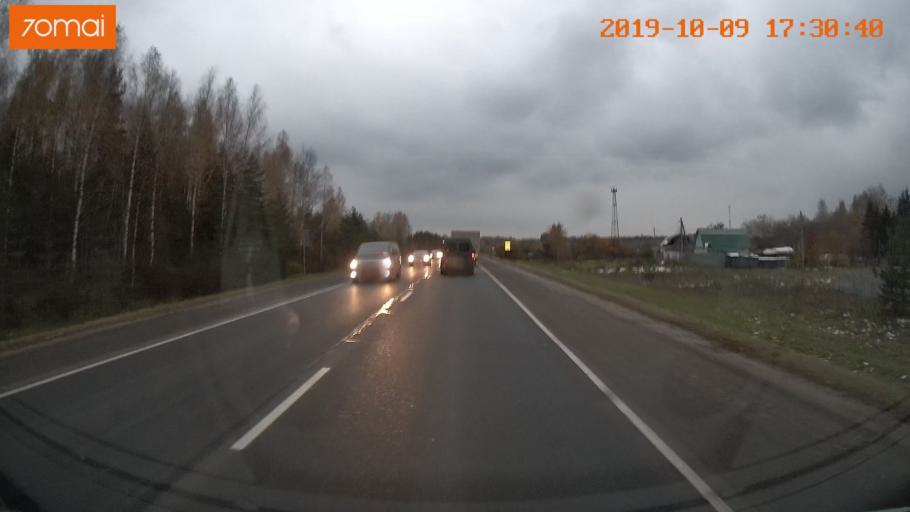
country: RU
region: Ivanovo
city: Bogorodskoye
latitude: 57.1410
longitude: 41.0470
